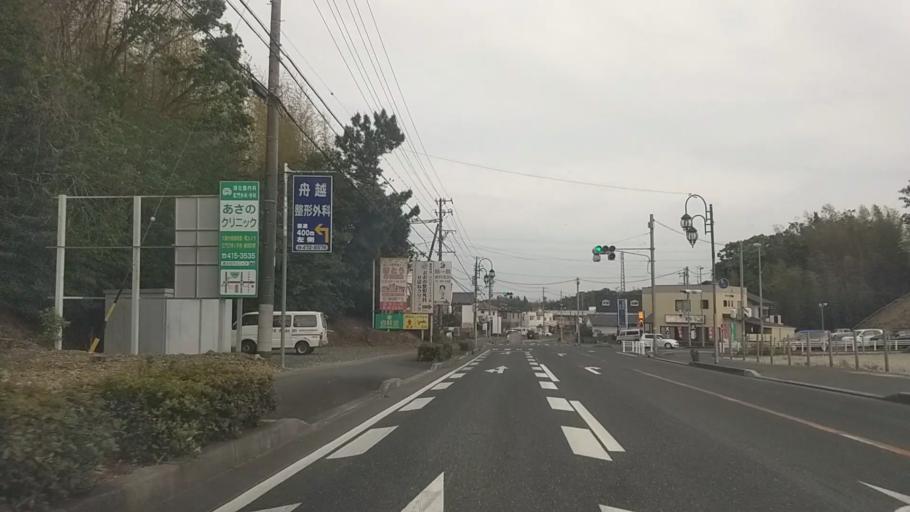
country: JP
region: Shizuoka
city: Hamamatsu
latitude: 34.7309
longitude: 137.6897
